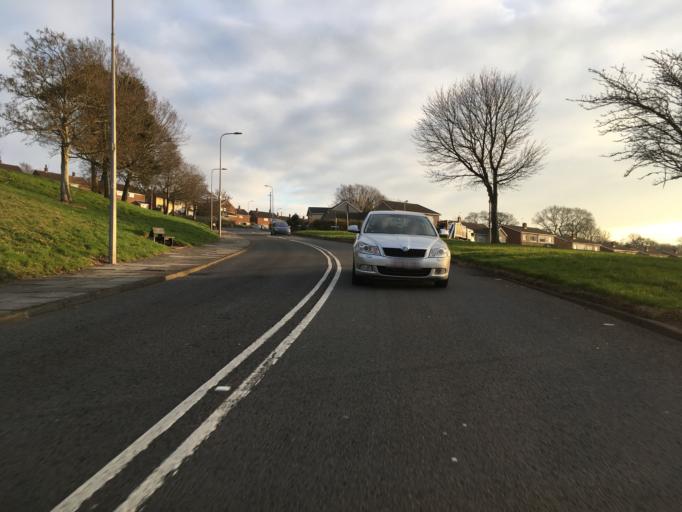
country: GB
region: Wales
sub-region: Cardiff
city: Cardiff
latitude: 51.5177
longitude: -3.1324
